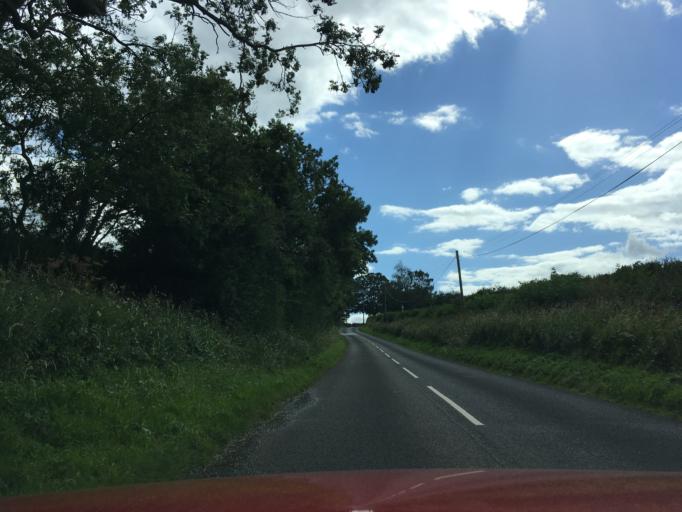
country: GB
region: England
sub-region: Nottinghamshire
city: East Leake
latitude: 52.8214
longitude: -1.2074
